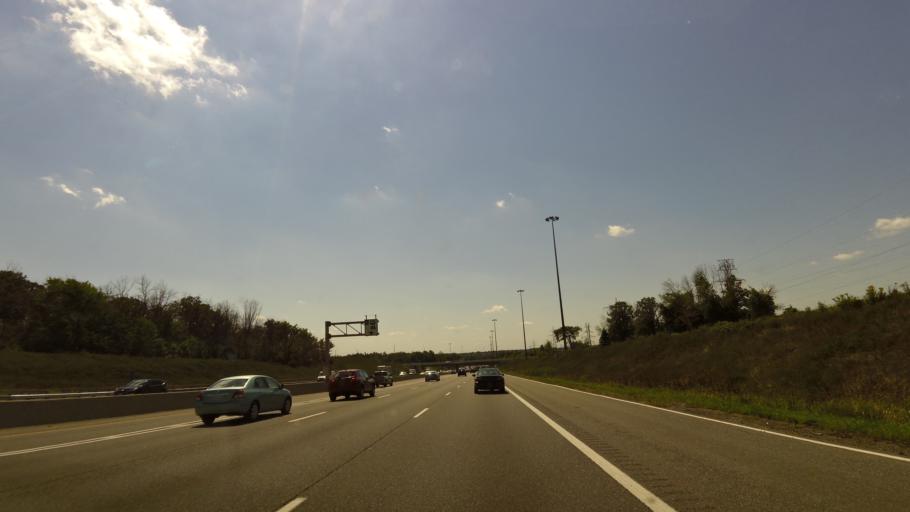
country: CA
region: Ontario
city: Mississauga
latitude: 43.5741
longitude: -79.6725
